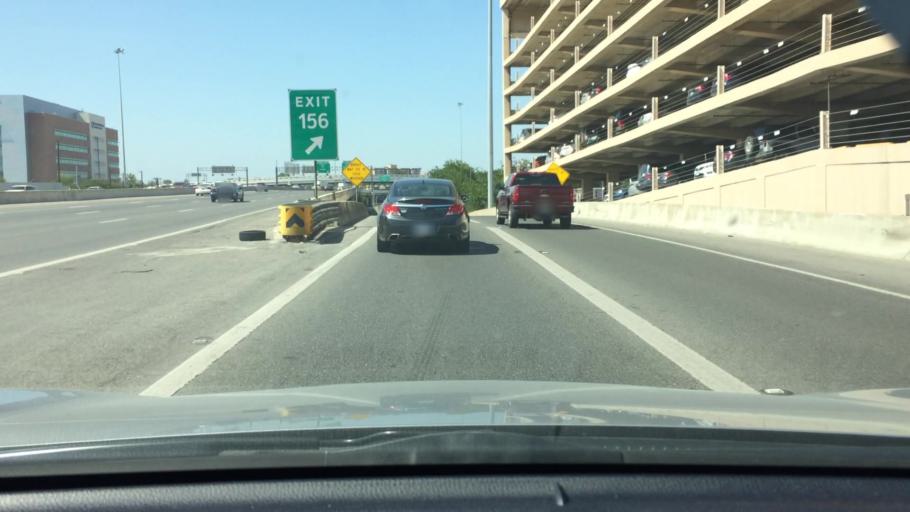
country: US
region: Texas
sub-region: Bexar County
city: San Antonio
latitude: 29.4275
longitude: -98.5007
